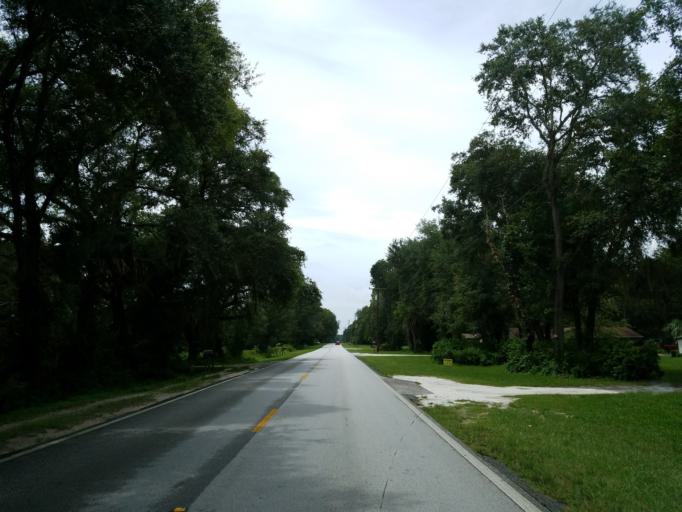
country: US
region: Florida
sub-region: Sumter County
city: Bushnell
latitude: 28.6689
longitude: -82.1707
